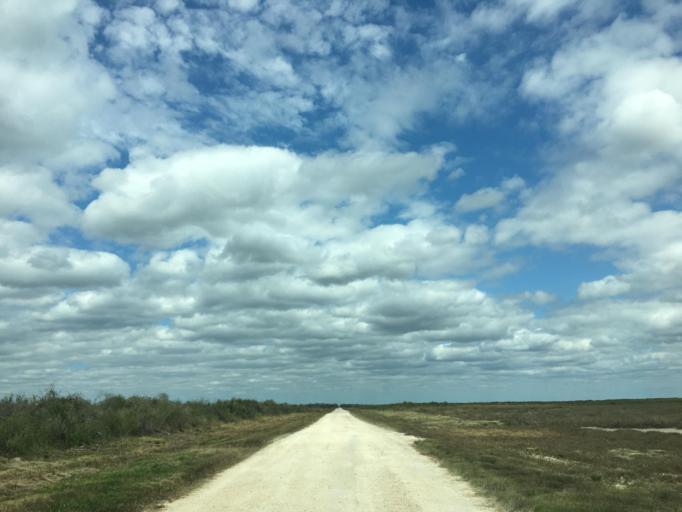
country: US
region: Texas
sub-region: Brazoria County
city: Oyster Creek
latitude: 29.0430
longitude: -95.2681
